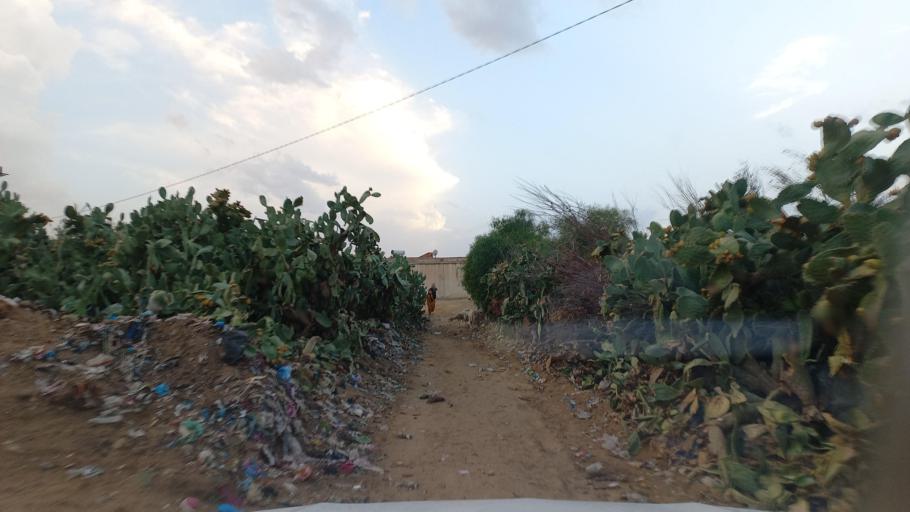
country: TN
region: Al Qasrayn
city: Kasserine
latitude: 35.2674
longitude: 9.0590
